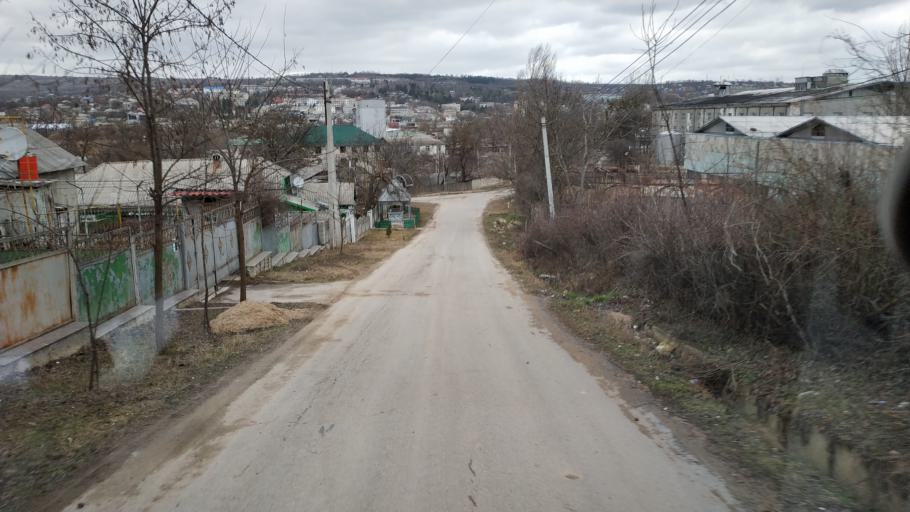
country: MD
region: Calarasi
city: Calarasi
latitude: 47.2415
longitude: 28.3107
